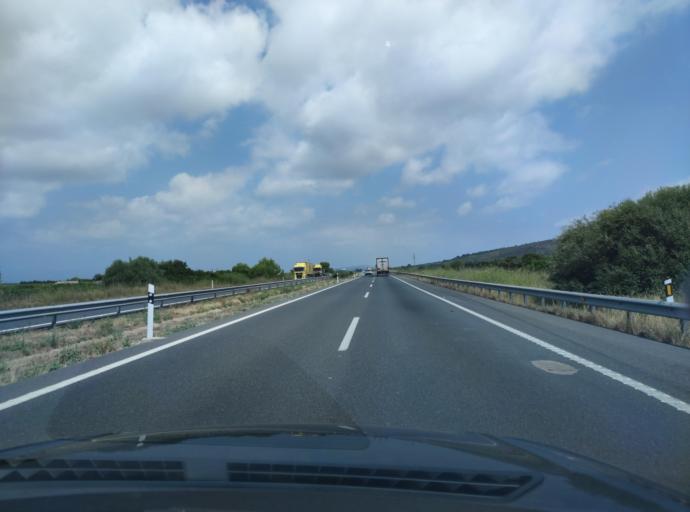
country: ES
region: Valencia
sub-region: Provincia de Castello
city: Vinaros
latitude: 40.4954
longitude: 0.4155
